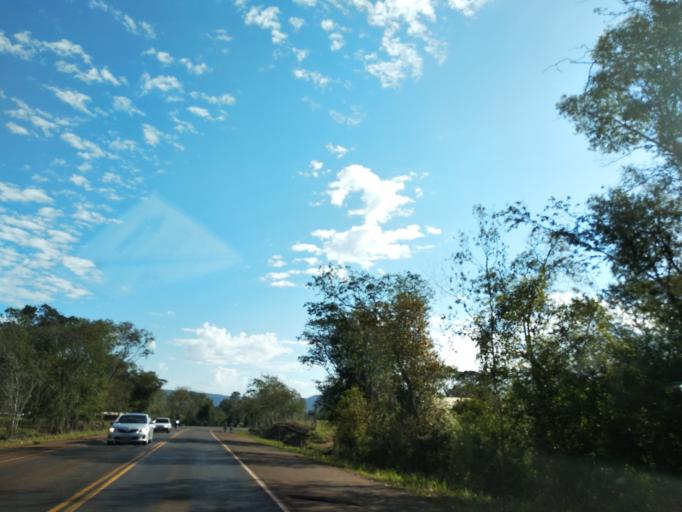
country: AR
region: Misiones
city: Aristobulo del Valle
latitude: -27.1023
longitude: -54.9650
